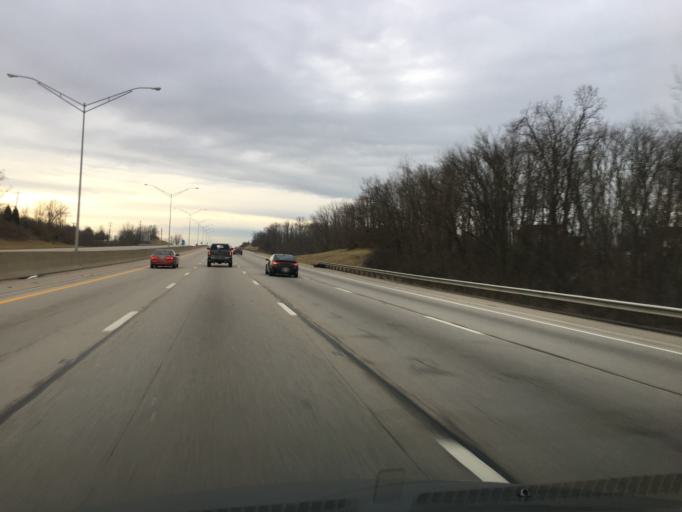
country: US
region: Kentucky
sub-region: Boone County
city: Walton
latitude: 38.9025
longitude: -84.6277
